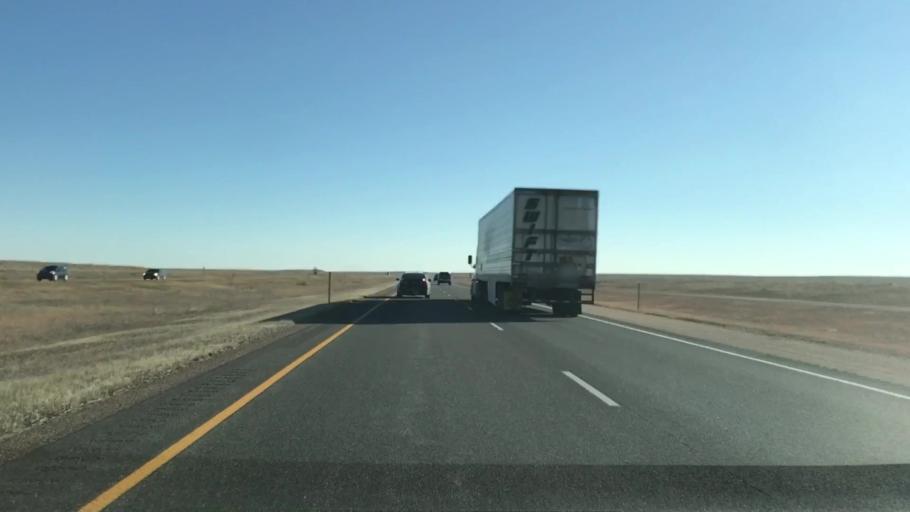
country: US
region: Colorado
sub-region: Lincoln County
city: Hugo
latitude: 39.2841
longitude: -103.2416
